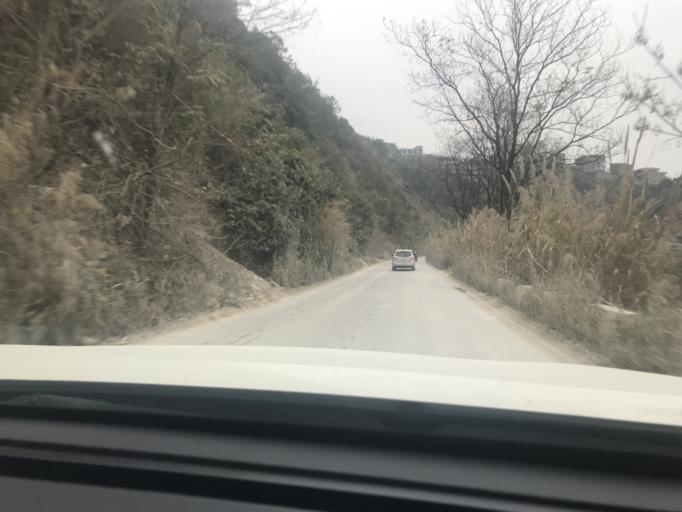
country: CN
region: Guangxi Zhuangzu Zizhiqu
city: Xinzhou
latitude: 24.9887
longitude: 105.8241
